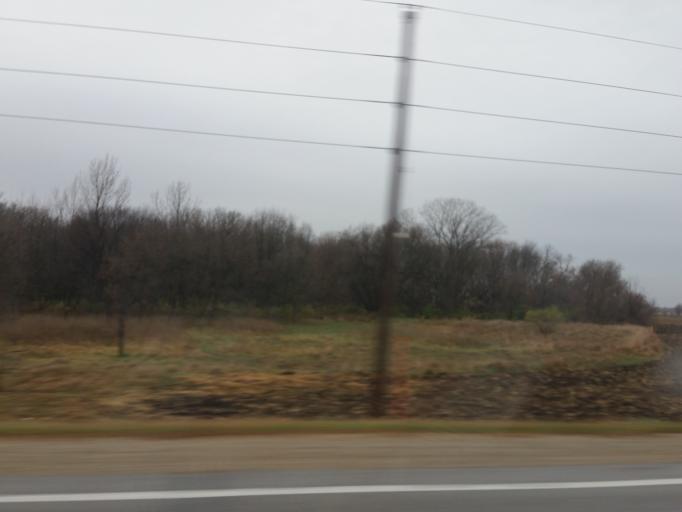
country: US
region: Iowa
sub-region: Black Hawk County
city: Elk Run Heights
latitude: 42.3902
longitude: -92.2497
